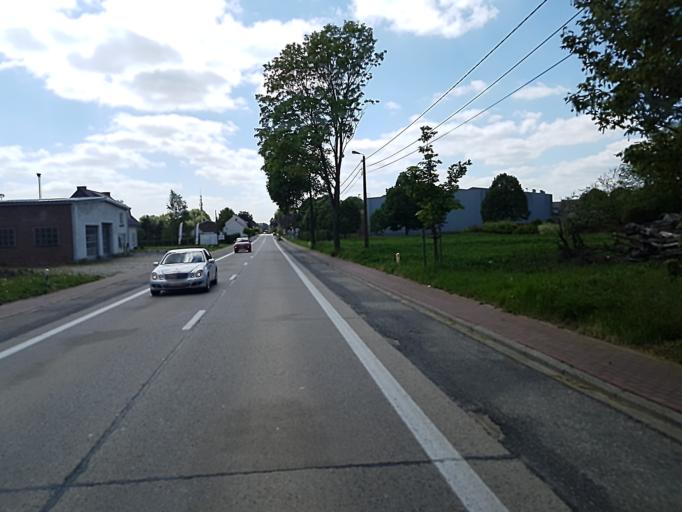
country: BE
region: Flanders
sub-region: Provincie Vlaams-Brabant
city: Glabbeek-Zuurbemde
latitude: 50.8715
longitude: 4.9602
